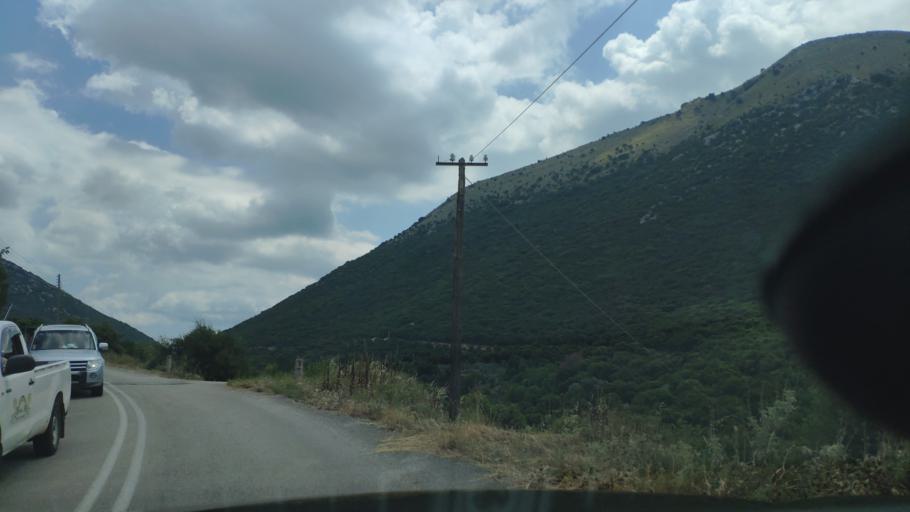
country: GR
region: Epirus
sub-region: Nomos Artas
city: Kampi
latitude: 39.2715
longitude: 20.9505
